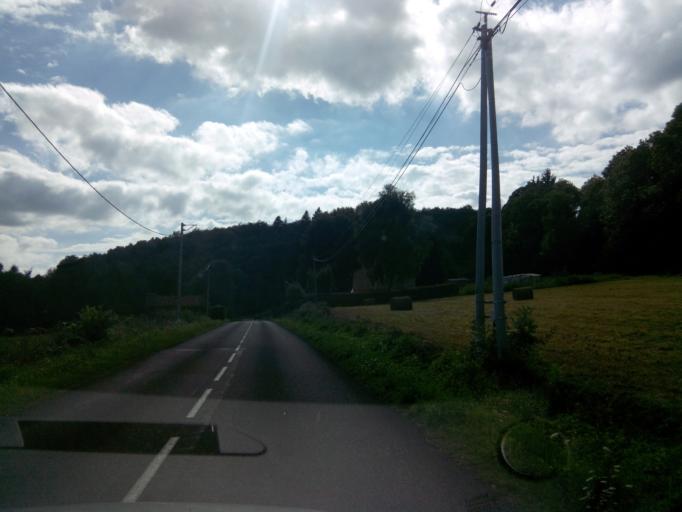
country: FR
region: Limousin
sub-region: Departement de la Haute-Vienne
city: Sauviat-sur-Vige
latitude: 45.8341
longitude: 1.6371
